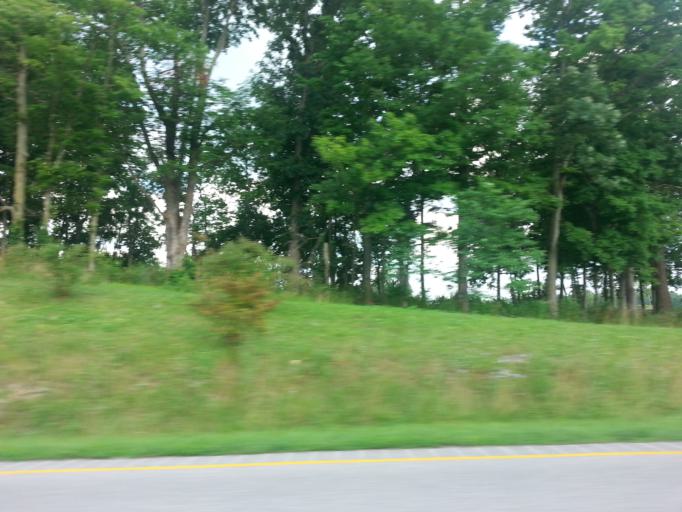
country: US
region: Kentucky
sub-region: Fayette County
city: Lexington-Fayette
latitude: 38.1105
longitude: -84.4040
